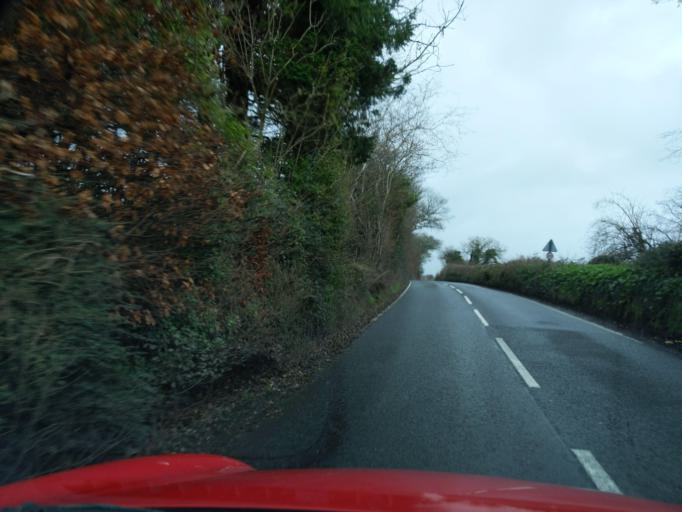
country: GB
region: England
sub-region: Cornwall
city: Launceston
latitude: 50.6452
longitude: -4.3559
